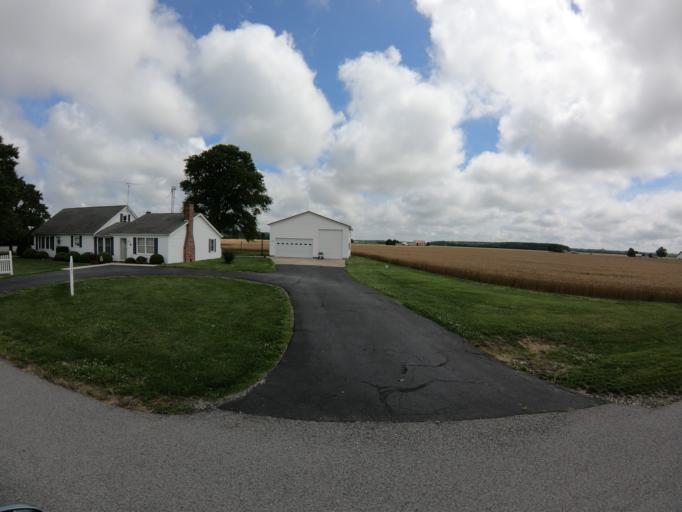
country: US
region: Maryland
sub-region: Caroline County
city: Greensboro
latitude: 39.0955
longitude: -75.8823
